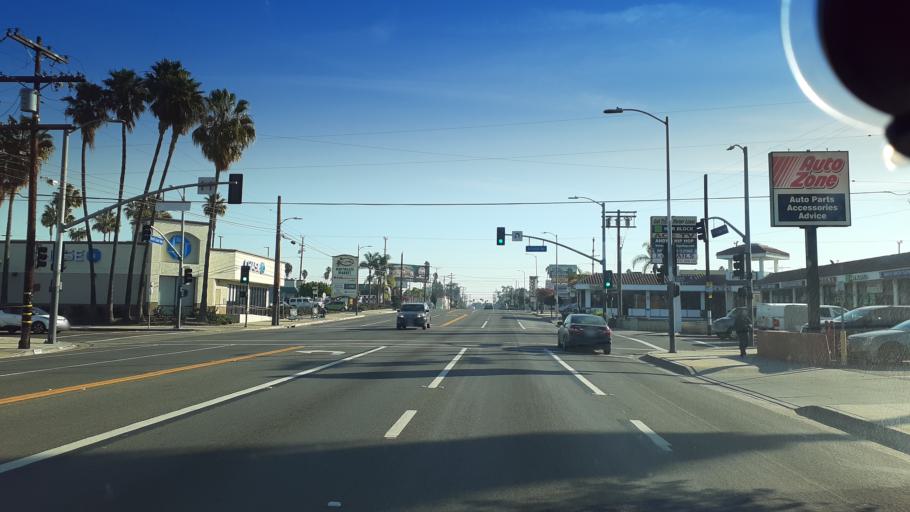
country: US
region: California
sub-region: Los Angeles County
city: West Carson
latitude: 33.7909
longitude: -118.2674
